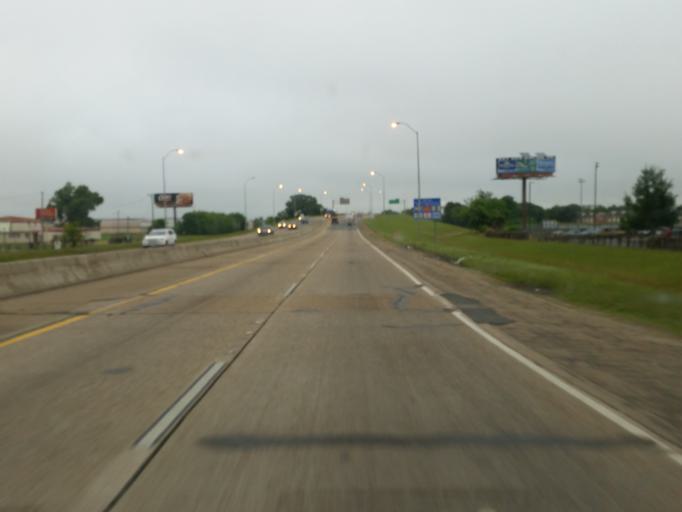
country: US
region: Louisiana
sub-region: Bossier Parish
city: Bossier City
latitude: 32.5205
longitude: -93.7074
